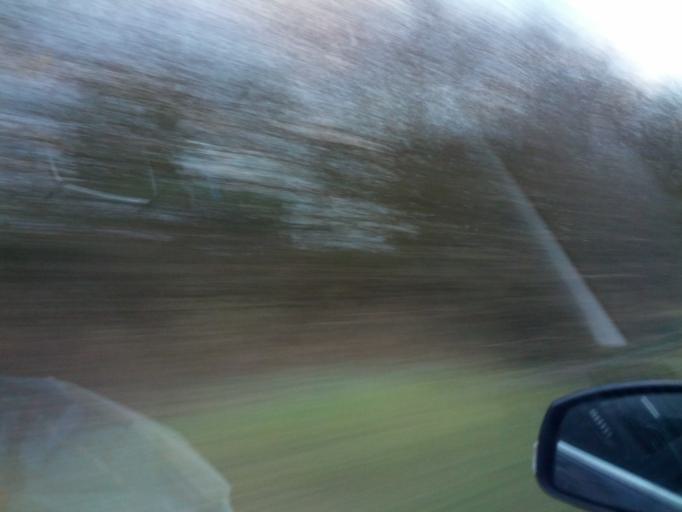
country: IE
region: Connaught
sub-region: County Galway
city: Athenry
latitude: 53.3185
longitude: -8.7624
